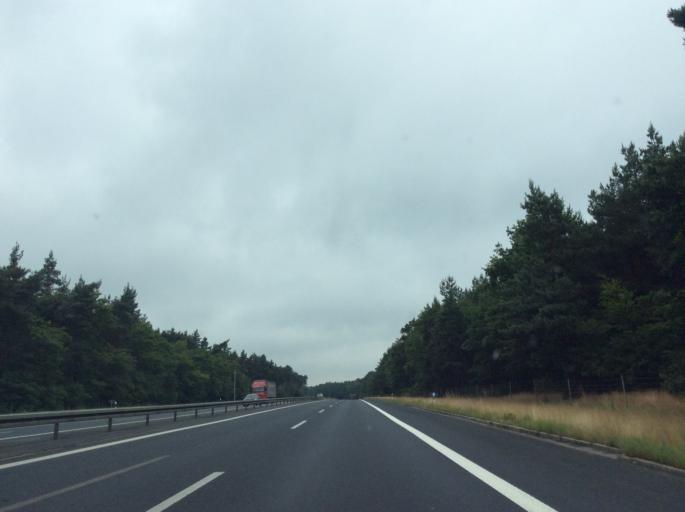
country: DE
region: Saxony
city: Radeburg
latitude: 51.2454
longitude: 13.7269
